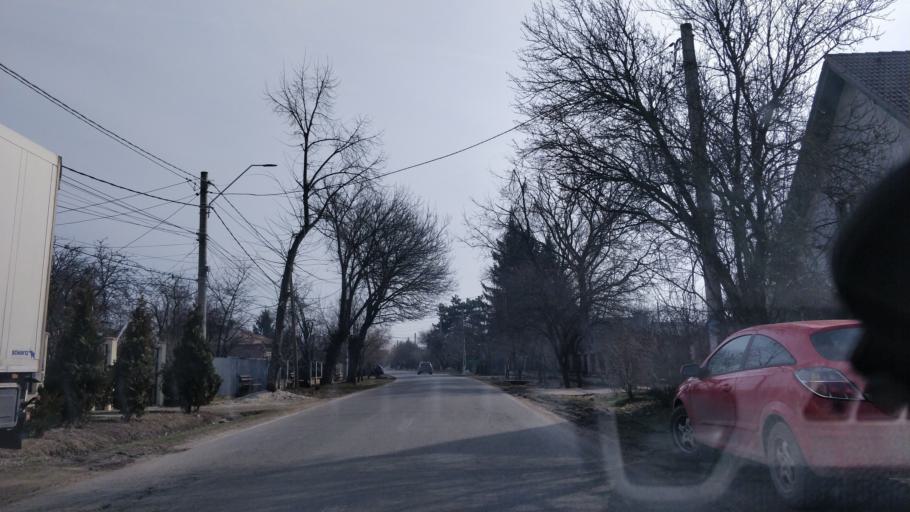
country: RO
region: Giurgiu
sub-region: Comuna Ulmi
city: Ulmi
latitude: 44.4652
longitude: 25.7742
